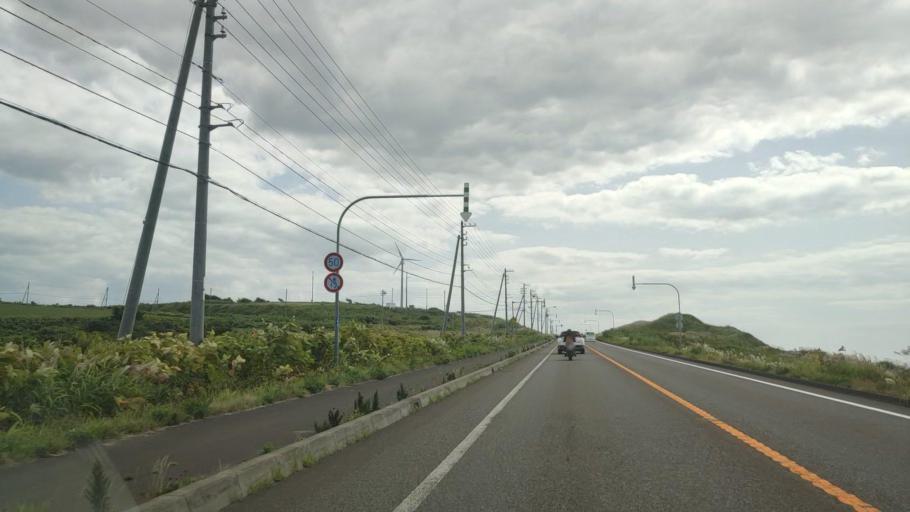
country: JP
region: Hokkaido
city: Rumoi
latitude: 44.5236
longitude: 141.7655
